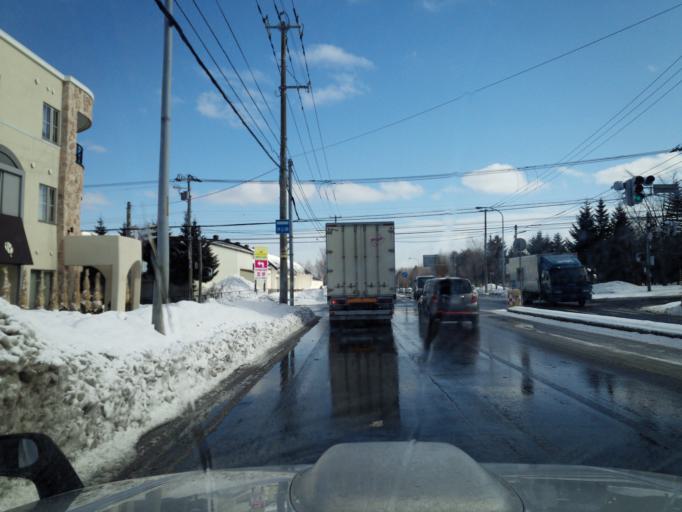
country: JP
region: Hokkaido
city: Kitahiroshima
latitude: 42.9914
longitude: 141.4531
